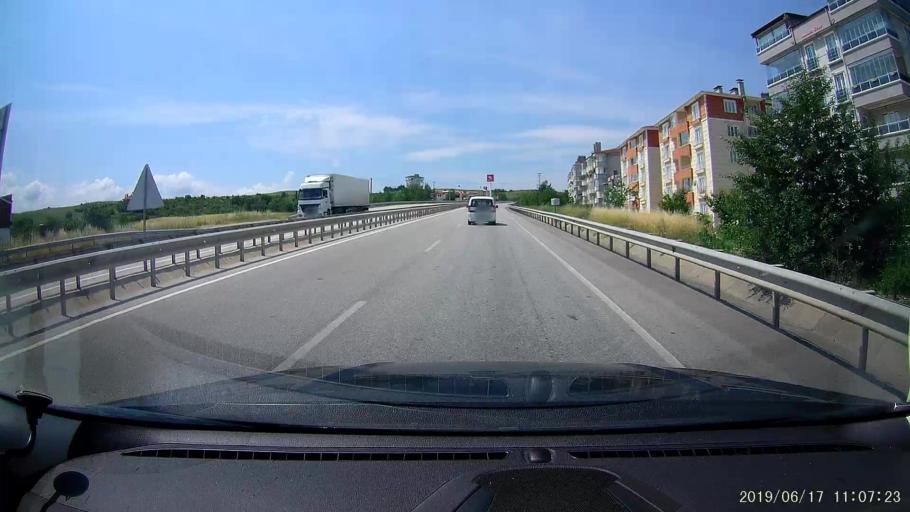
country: TR
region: Kastamonu
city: Tosya
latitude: 41.0032
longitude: 34.0551
